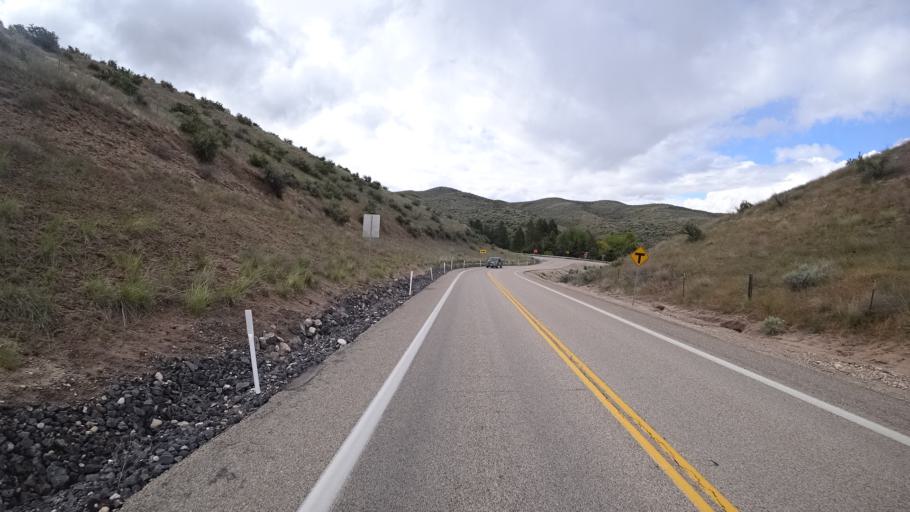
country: US
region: Idaho
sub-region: Ada County
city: Garden City
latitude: 43.6940
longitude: -116.2267
